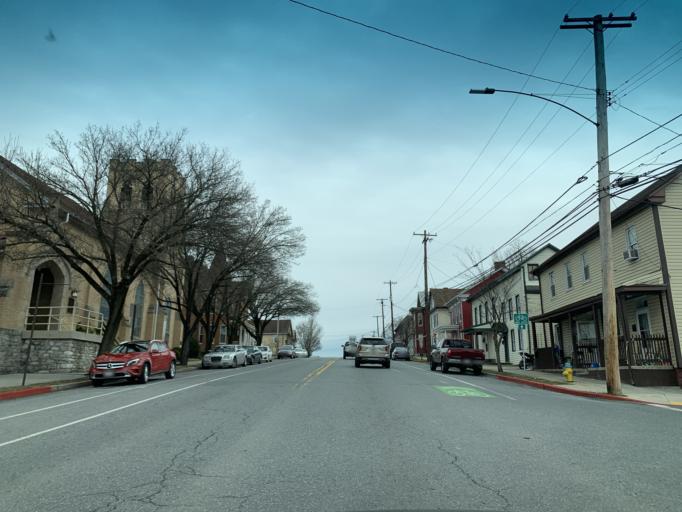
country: US
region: Maryland
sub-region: Washington County
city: Williamsport
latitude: 39.6005
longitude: -77.8238
